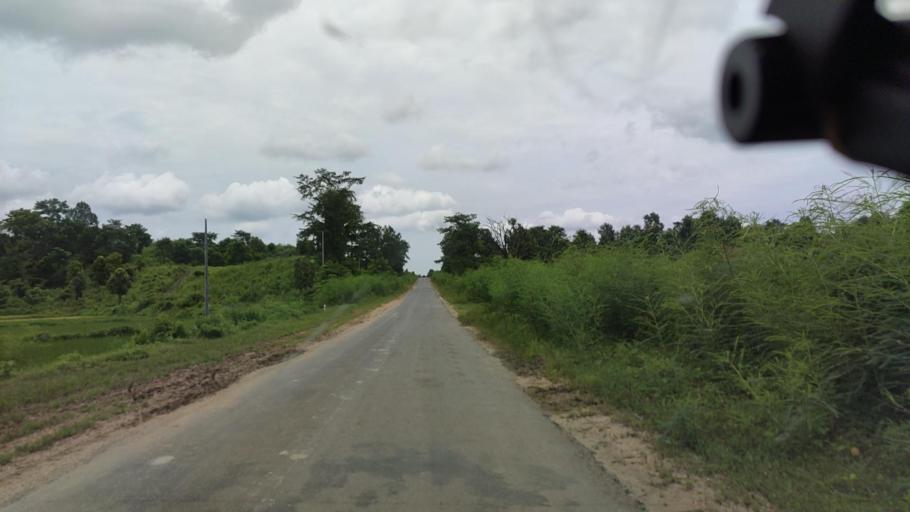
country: MM
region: Bago
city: Pyay
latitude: 18.8200
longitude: 95.0083
